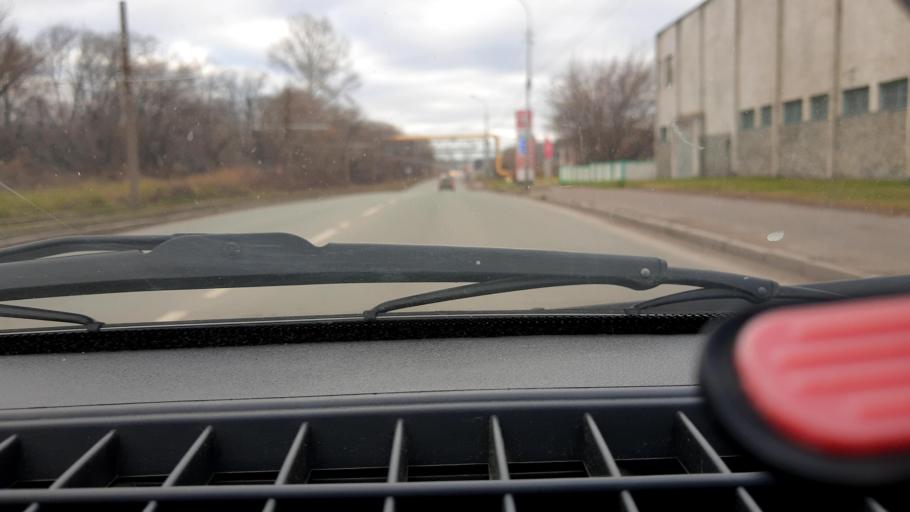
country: RU
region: Bashkortostan
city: Ufa
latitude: 54.7984
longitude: 56.1184
